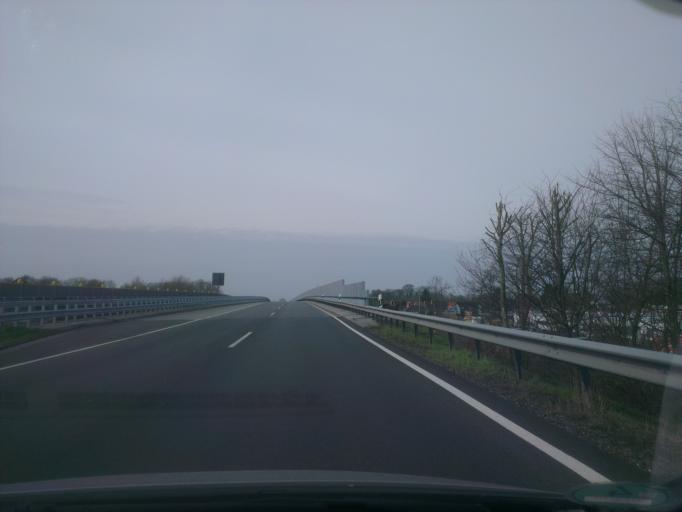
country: DE
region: Lower Saxony
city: Emden
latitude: 53.3882
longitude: 7.2106
